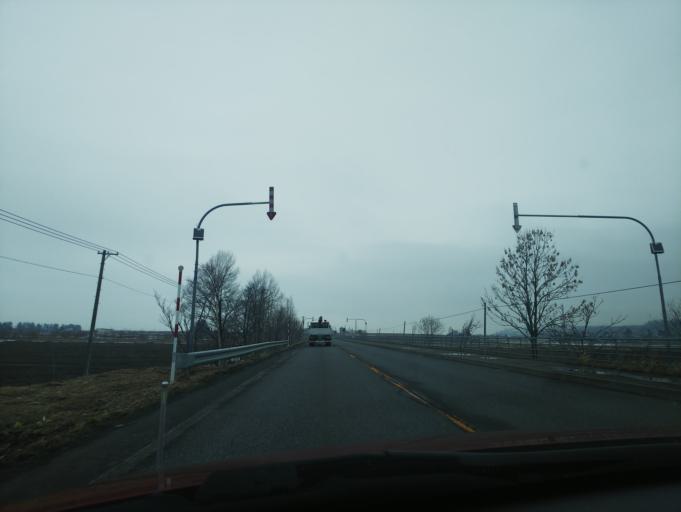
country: JP
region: Hokkaido
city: Nayoro
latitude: 44.0659
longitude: 142.3981
